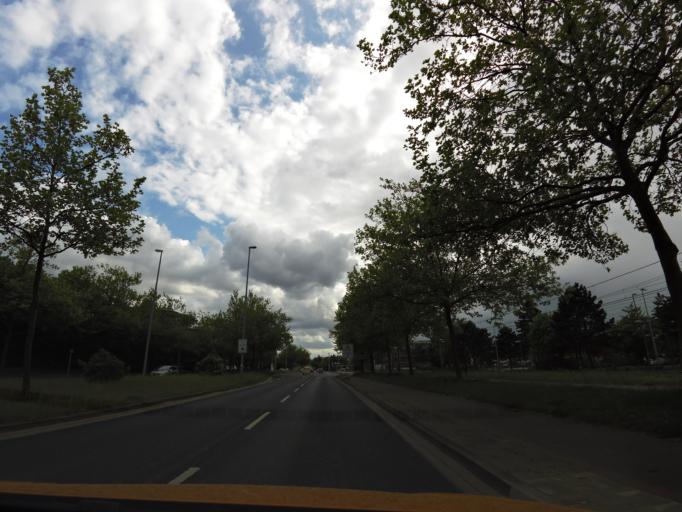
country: DE
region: Lower Saxony
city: Laatzen
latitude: 52.3812
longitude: 9.8095
